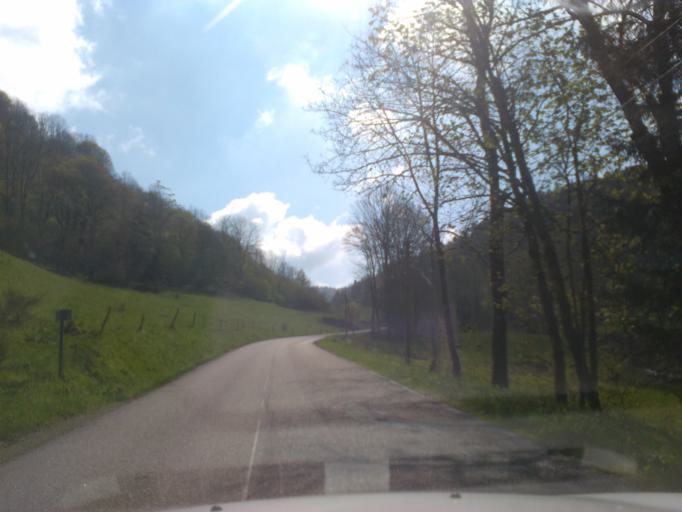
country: FR
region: Lorraine
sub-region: Departement des Vosges
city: Saulxures-sur-Moselotte
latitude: 47.9877
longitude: 6.7861
